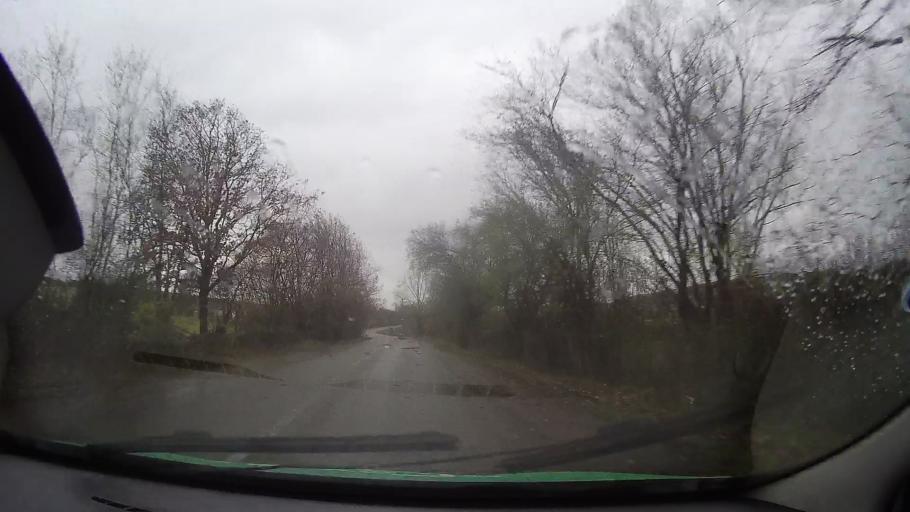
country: RO
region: Mures
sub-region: Comuna Brancovenesti
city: Valenii de Mures
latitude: 46.9196
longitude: 24.7766
